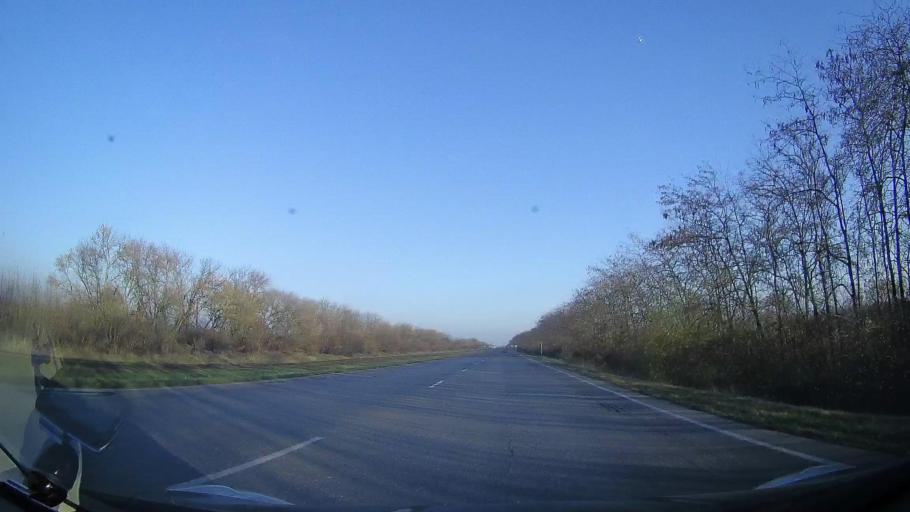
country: RU
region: Rostov
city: Kirovskaya
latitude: 47.0031
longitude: 39.9707
